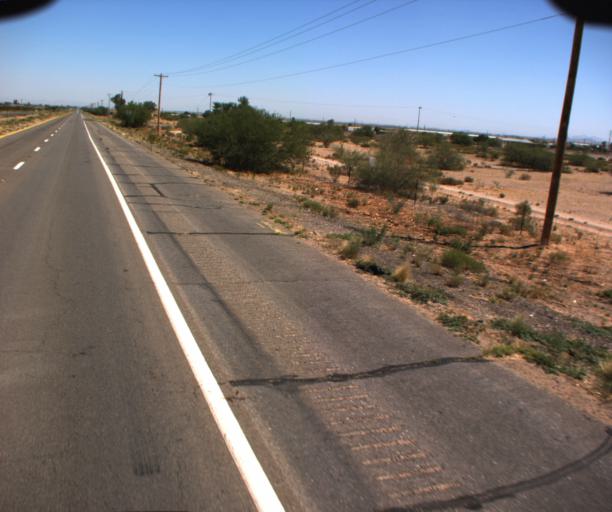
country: US
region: Arizona
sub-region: Pinal County
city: Maricopa
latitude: 32.8873
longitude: -112.0493
